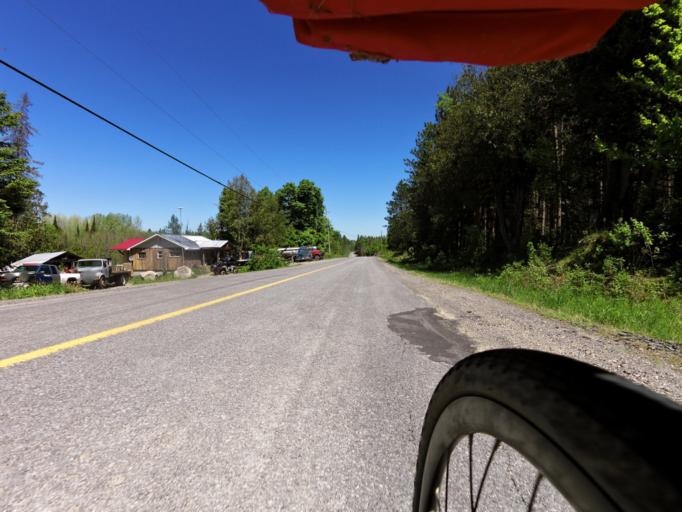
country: CA
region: Ontario
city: Carleton Place
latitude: 45.1758
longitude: -76.4073
